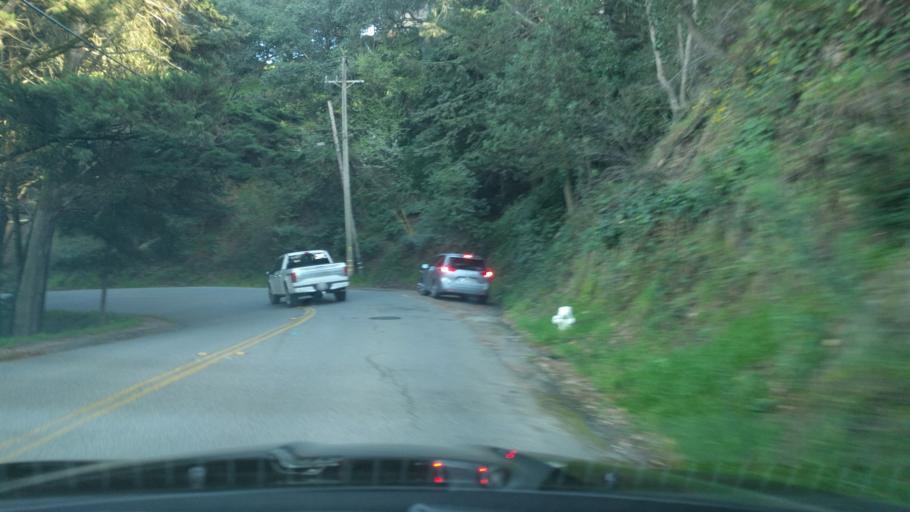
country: US
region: California
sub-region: Alameda County
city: Piedmont
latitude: 37.8306
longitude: -122.1874
